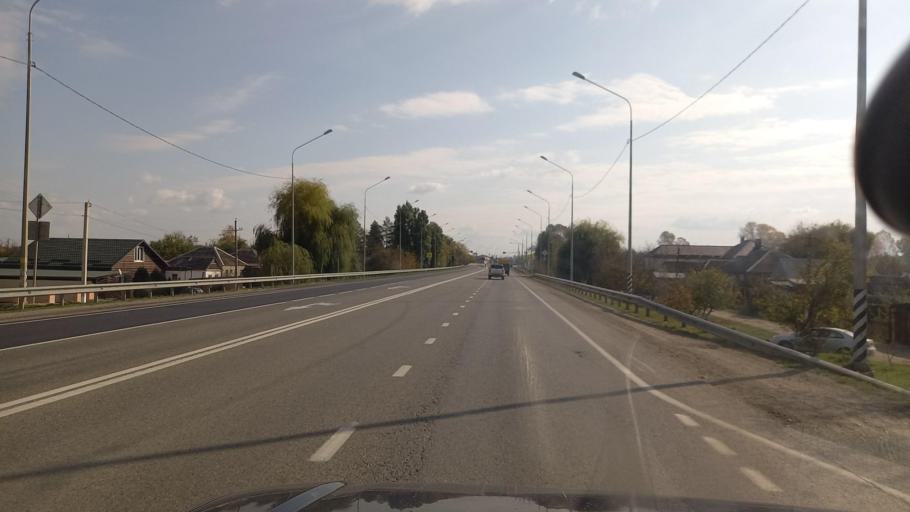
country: RU
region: Krasnodarskiy
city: Novoukrainskiy
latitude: 44.8956
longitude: 38.0550
